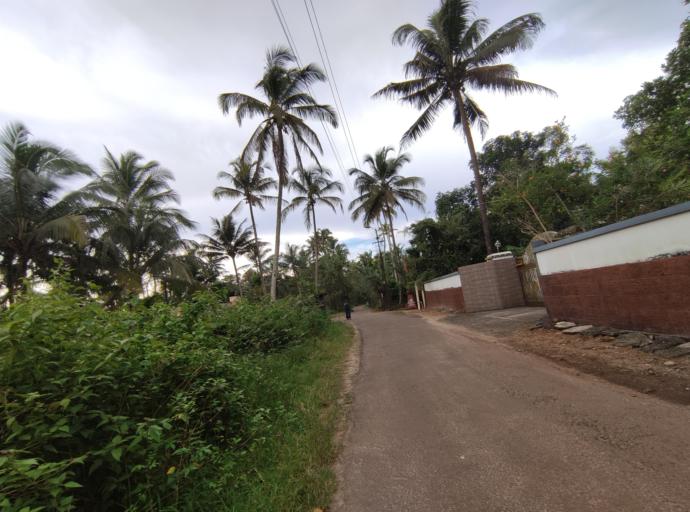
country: IN
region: Kerala
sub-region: Alappuzha
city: Shertallai
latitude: 9.6702
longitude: 76.3487
